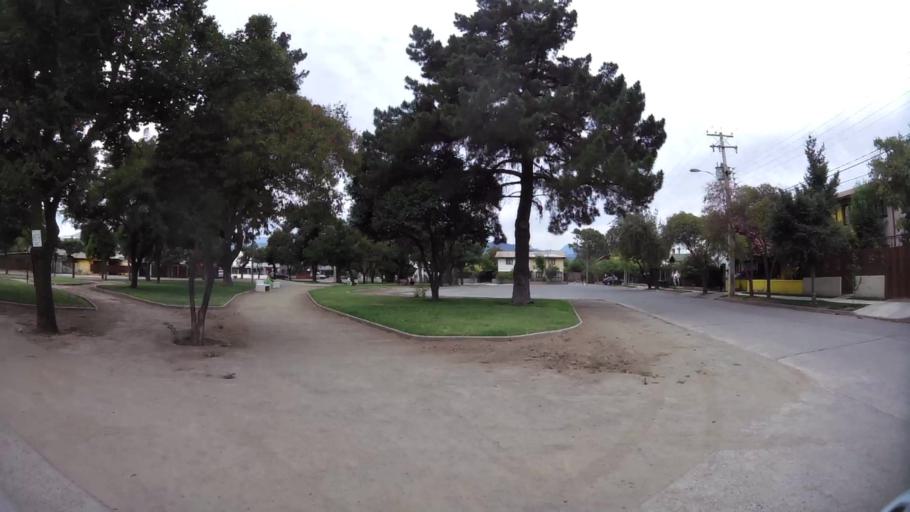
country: CL
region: O'Higgins
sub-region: Provincia de Cachapoal
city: Rancagua
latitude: -34.1569
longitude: -70.7373
